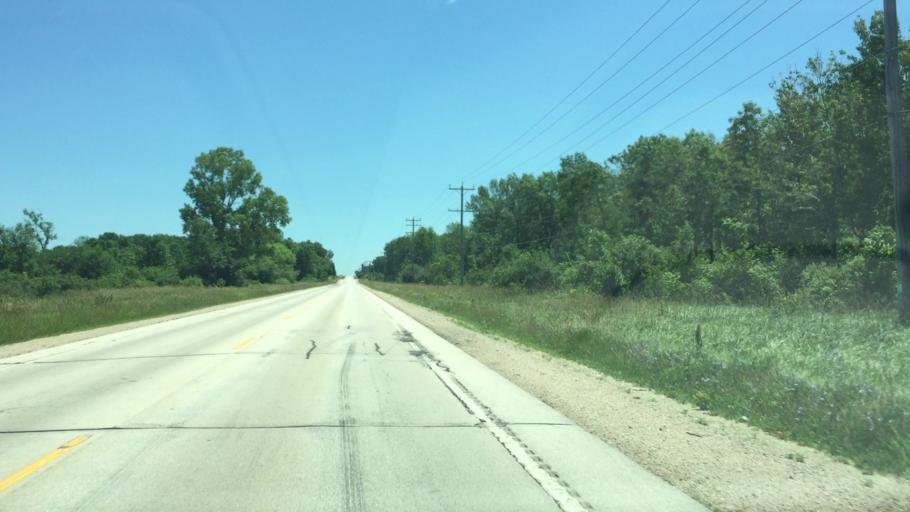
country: US
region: Wisconsin
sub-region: Calumet County
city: Sherwood
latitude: 44.1409
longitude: -88.2531
